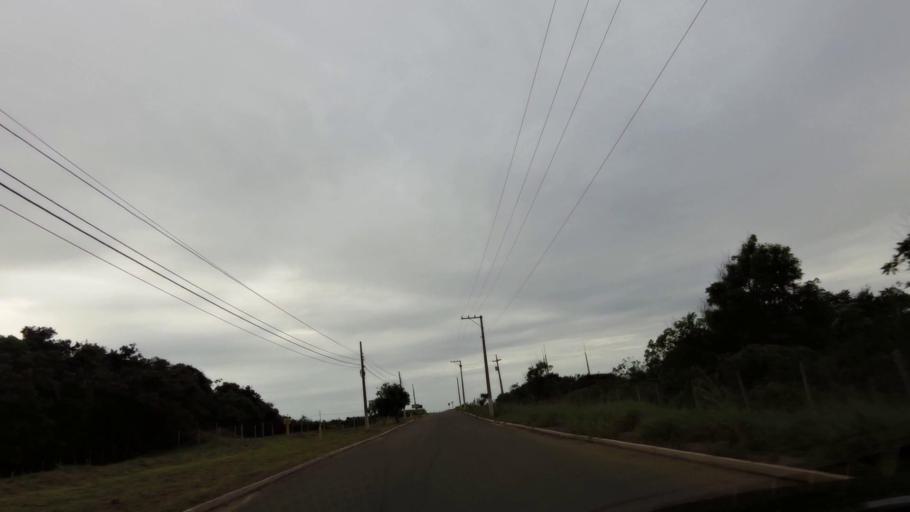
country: BR
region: Espirito Santo
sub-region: Piuma
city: Piuma
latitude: -20.7999
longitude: -40.5851
